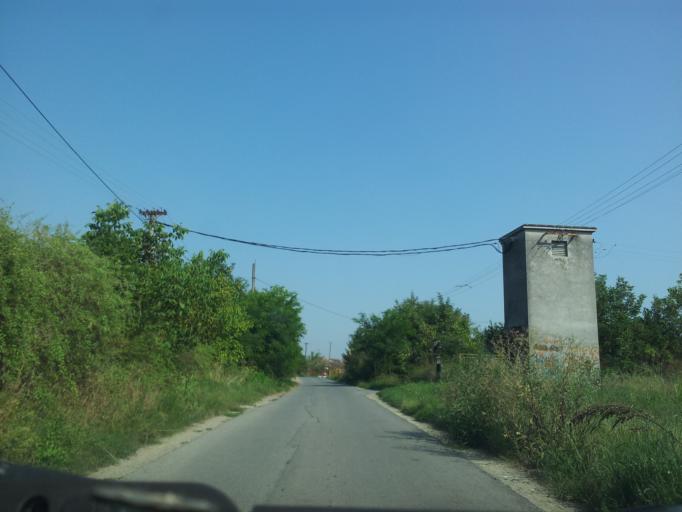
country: HR
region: Osjecko-Baranjska
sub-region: Grad Osijek
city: Osijek
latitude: 45.5553
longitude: 18.7402
